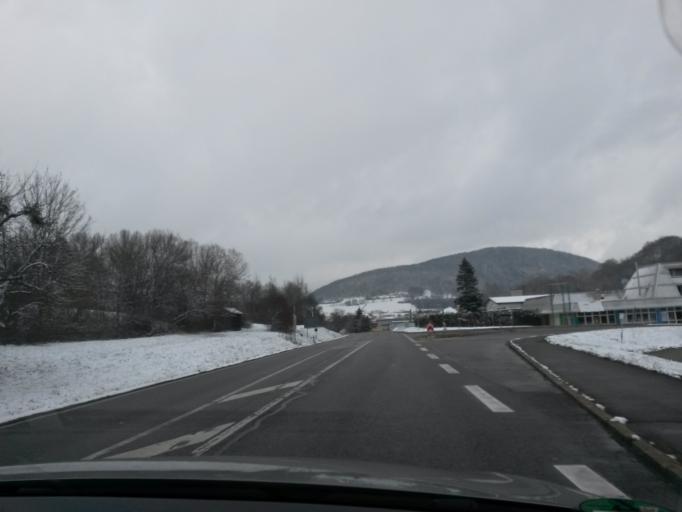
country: DE
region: Baden-Wuerttemberg
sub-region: Regierungsbezirk Stuttgart
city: Deggingen
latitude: 48.6016
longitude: 9.7285
